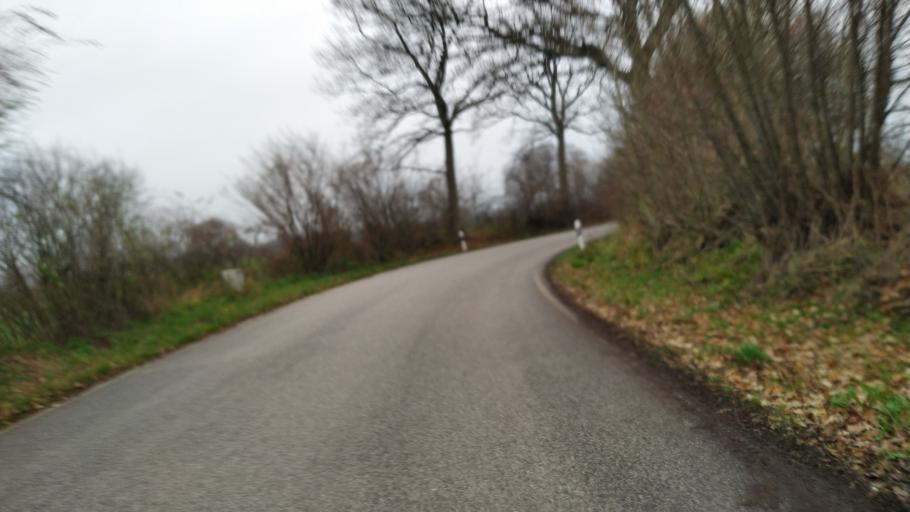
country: DE
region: Schleswig-Holstein
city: Travemuende
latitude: 53.9629
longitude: 10.8347
